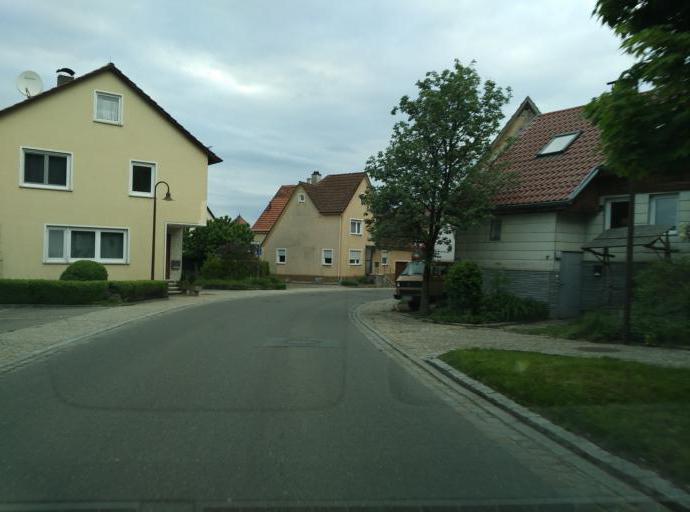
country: DE
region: Baden-Wuerttemberg
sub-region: Regierungsbezirk Stuttgart
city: Beuren
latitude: 48.5656
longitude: 9.3894
